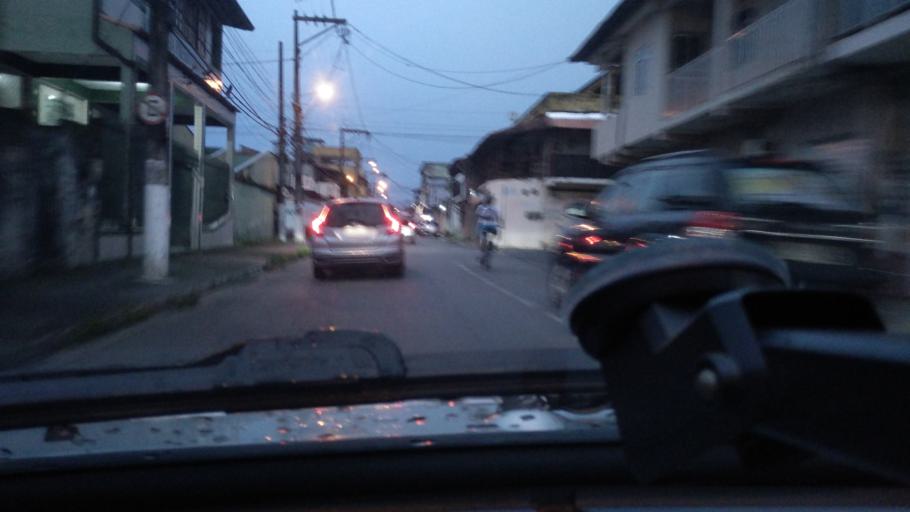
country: BR
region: Rio de Janeiro
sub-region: Angra Dos Reis
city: Angra dos Reis
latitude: -23.0152
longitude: -44.5357
